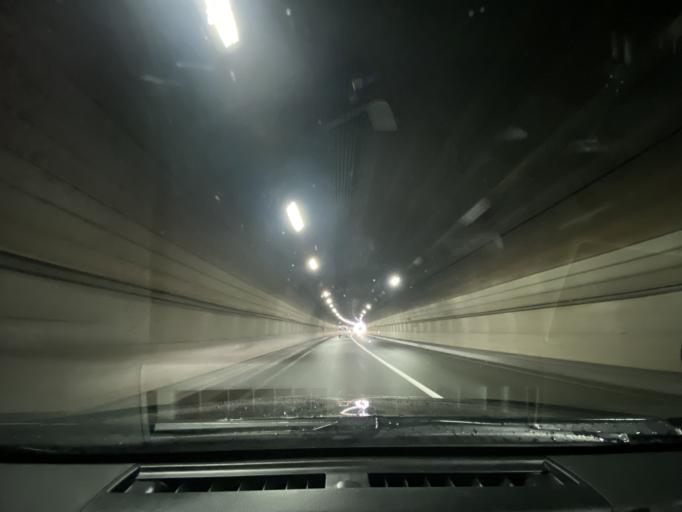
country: JP
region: Hokkaido
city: Fukagawa
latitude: 43.7298
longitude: 142.2014
